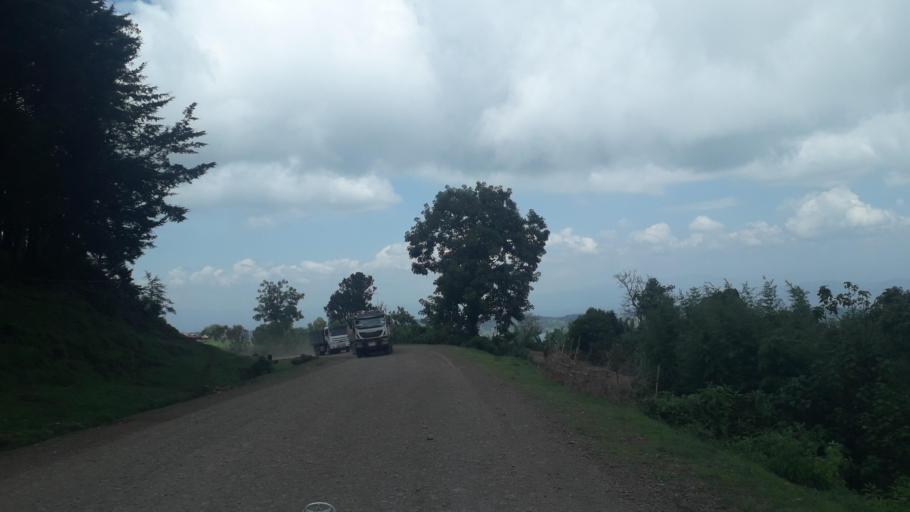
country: ET
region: Oromiya
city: Jima
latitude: 7.4497
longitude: 36.8740
